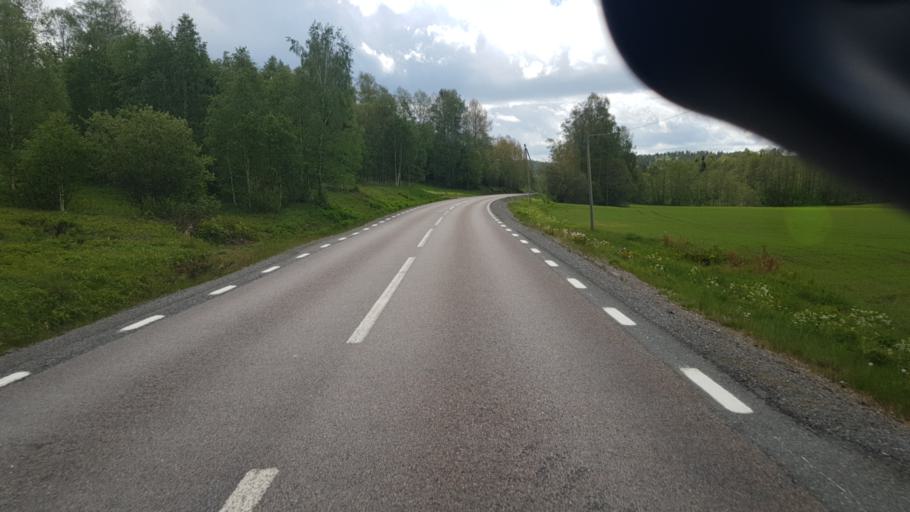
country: SE
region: Vaermland
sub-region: Arjangs Kommun
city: Arjaeng
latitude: 59.6053
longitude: 12.1522
